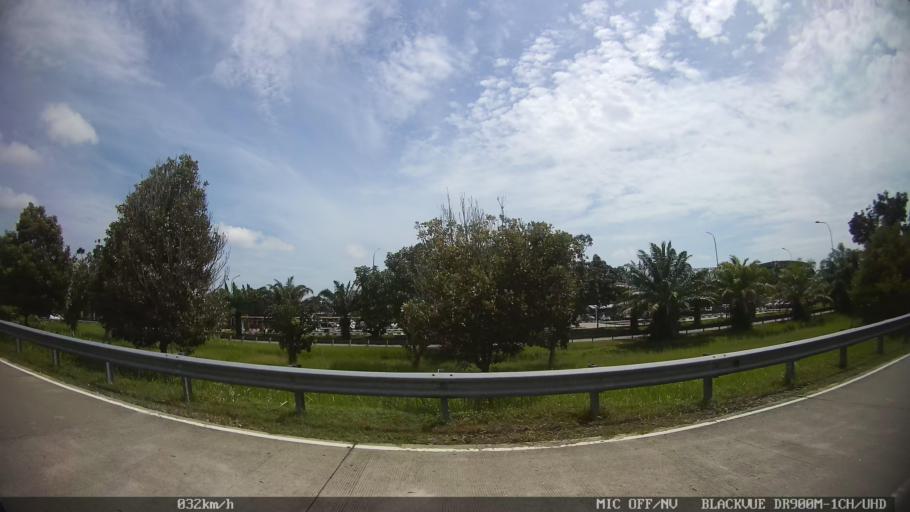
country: ID
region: North Sumatra
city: Percut
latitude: 3.6340
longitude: 98.8765
